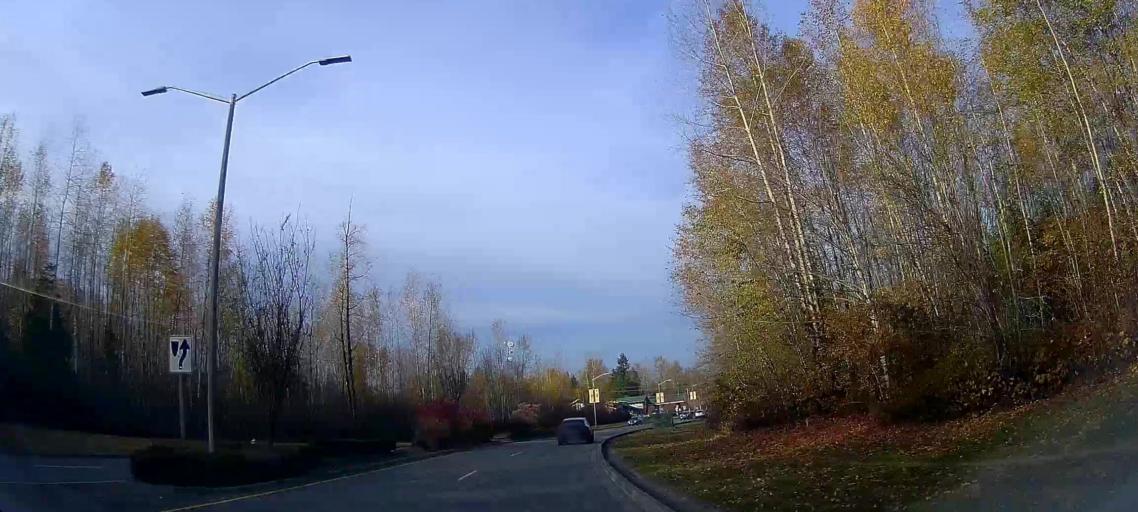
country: US
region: Washington
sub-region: Snohomish County
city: Marysville
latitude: 48.0970
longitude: -122.1916
